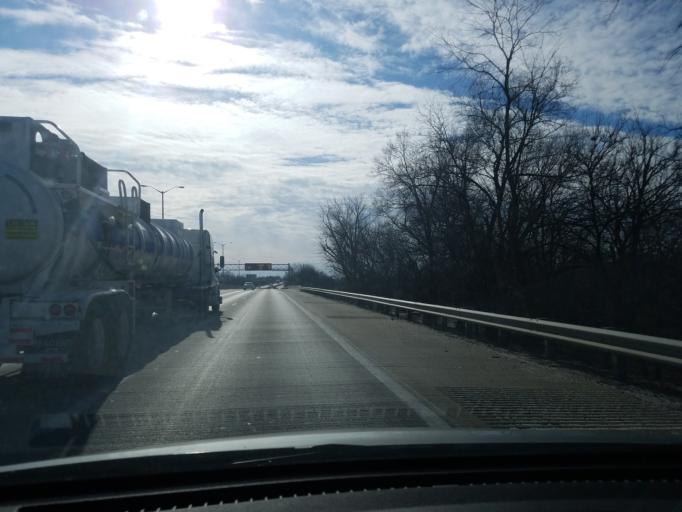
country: US
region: Kentucky
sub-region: Jefferson County
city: Shively
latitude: 38.2393
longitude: -85.8163
